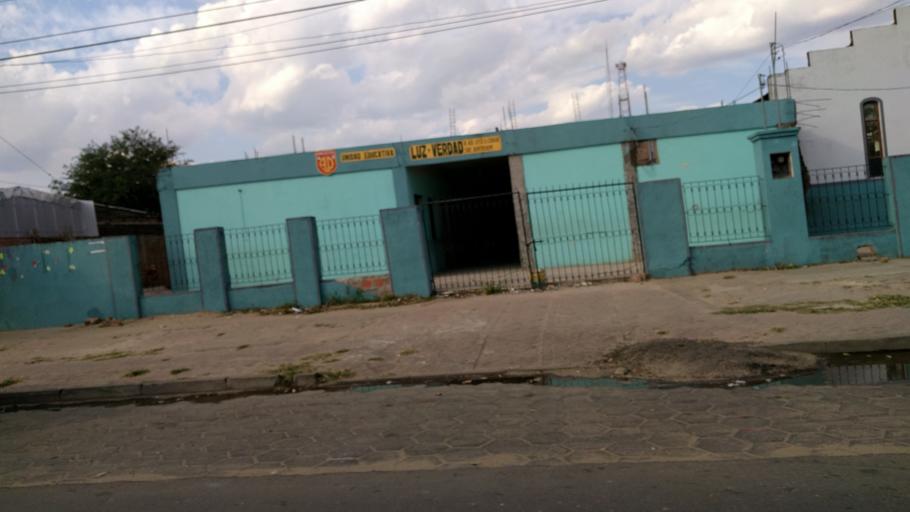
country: BO
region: Santa Cruz
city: Warnes
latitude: -17.5094
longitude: -63.1682
